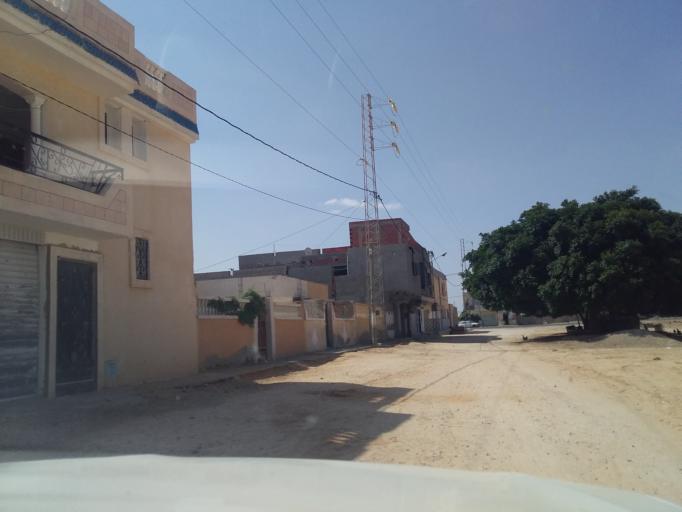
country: TN
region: Madanin
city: Medenine
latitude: 33.6053
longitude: 10.3039
